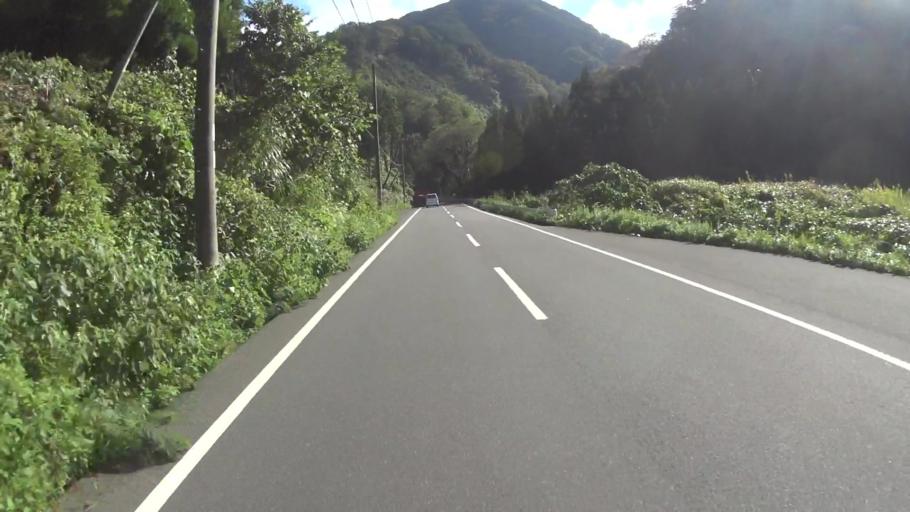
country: JP
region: Kyoto
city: Miyazu
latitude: 35.6401
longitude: 135.1277
